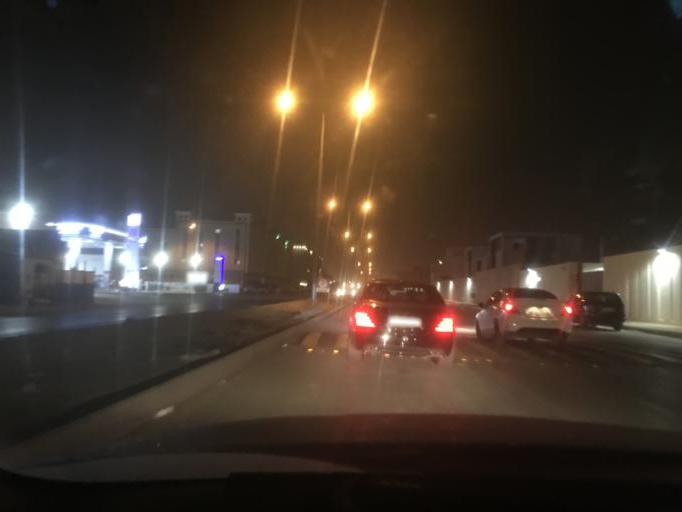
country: SA
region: Ar Riyad
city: Riyadh
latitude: 24.8290
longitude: 46.7350
